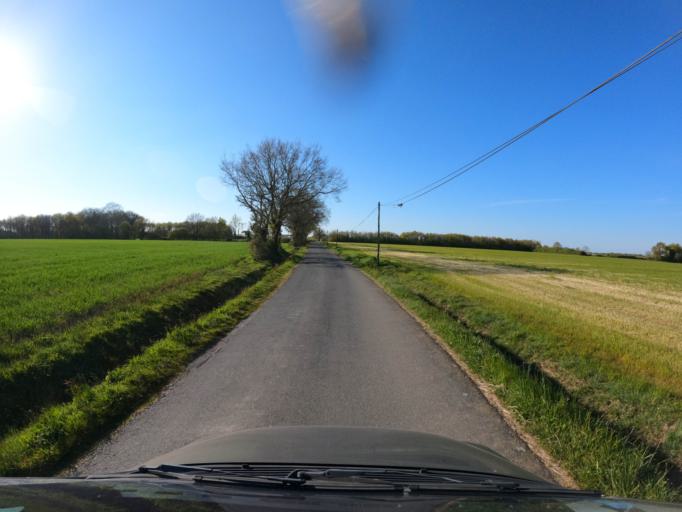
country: FR
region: Pays de la Loire
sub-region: Departement de la Vendee
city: Les Brouzils
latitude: 46.8966
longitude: -1.3691
